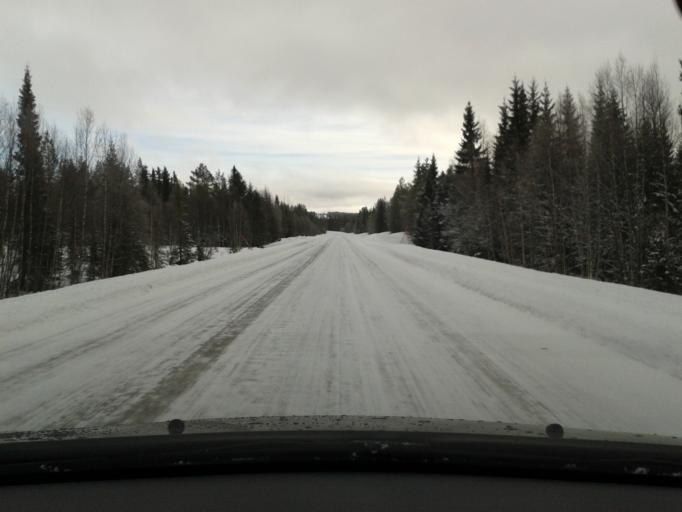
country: SE
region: Vaesterbotten
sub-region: Vilhelmina Kommun
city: Sjoberg
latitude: 64.8057
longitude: 15.9912
